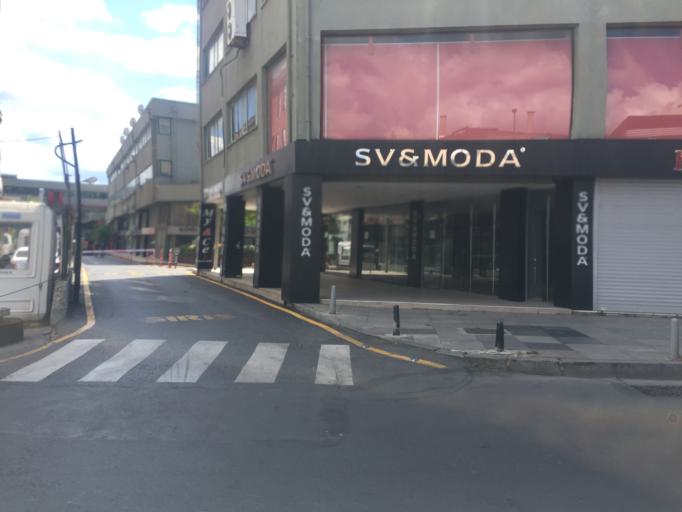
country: TR
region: Istanbul
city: merter keresteciler
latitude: 41.0295
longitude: 28.9158
